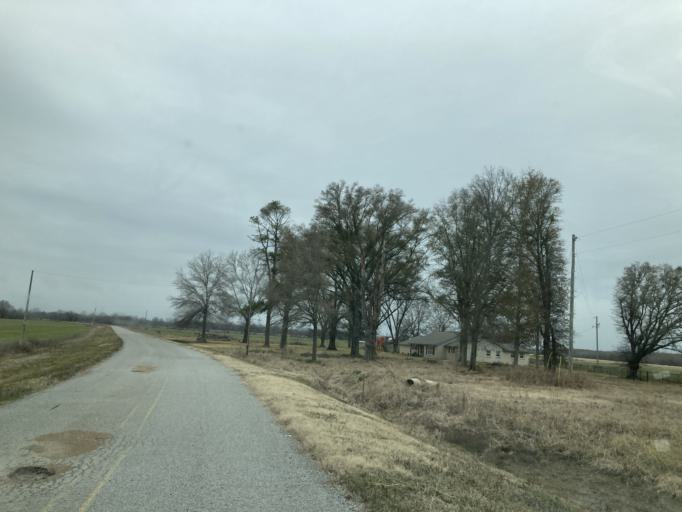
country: US
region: Mississippi
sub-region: Yazoo County
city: Yazoo City
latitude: 33.0110
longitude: -90.4707
